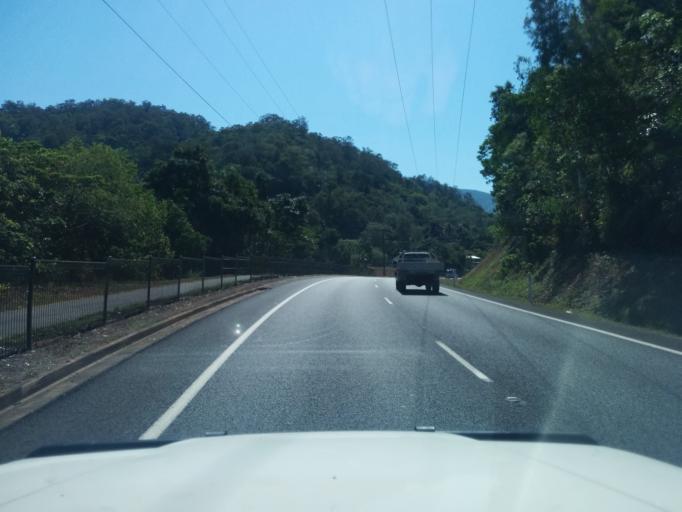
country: AU
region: Queensland
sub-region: Cairns
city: Redlynch
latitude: -16.9137
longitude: 145.7196
